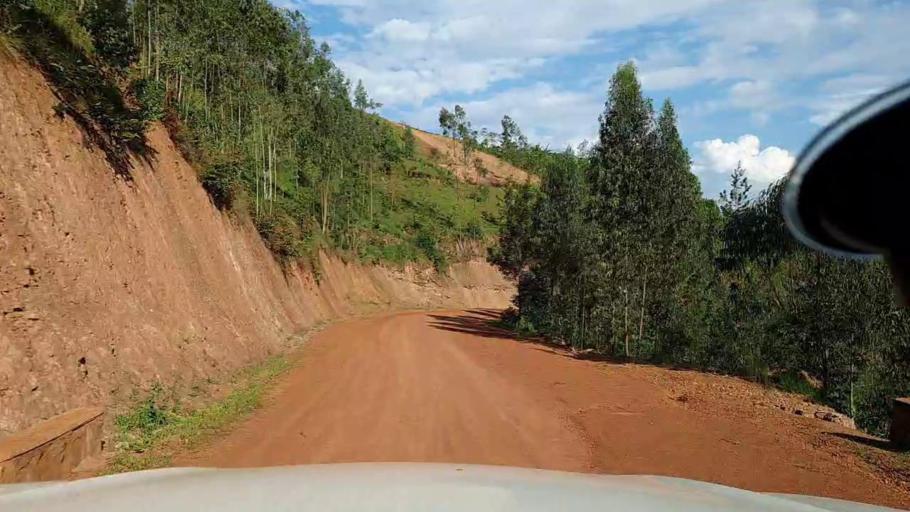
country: RW
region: Kigali
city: Kigali
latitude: -1.8468
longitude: 29.8619
